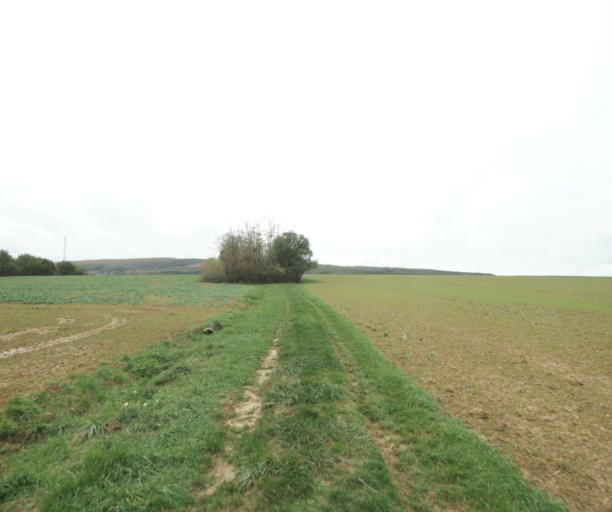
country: FR
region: Bourgogne
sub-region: Departement de Saone-et-Loire
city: Saint-Martin-Belle-Roche
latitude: 46.4589
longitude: 4.8679
